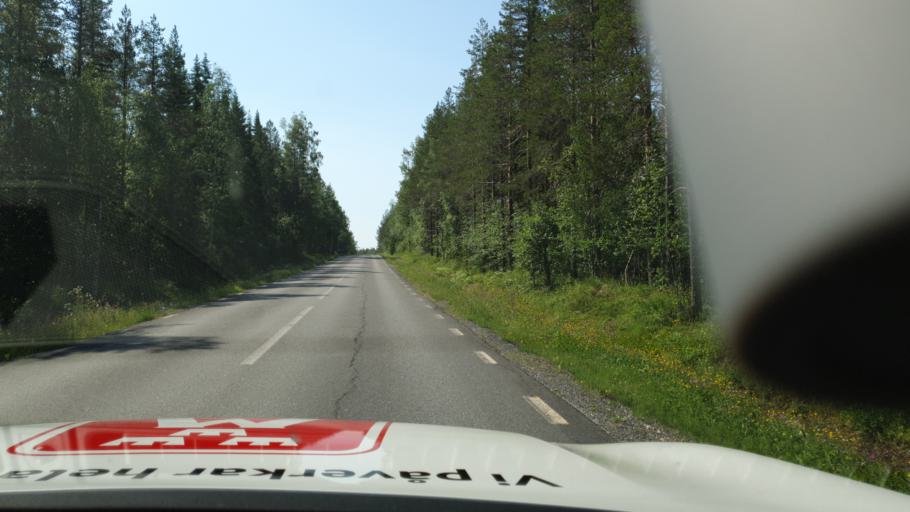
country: SE
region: Vaesterbotten
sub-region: Skelleftea Kommun
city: Langsele
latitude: 64.9726
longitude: 20.0497
